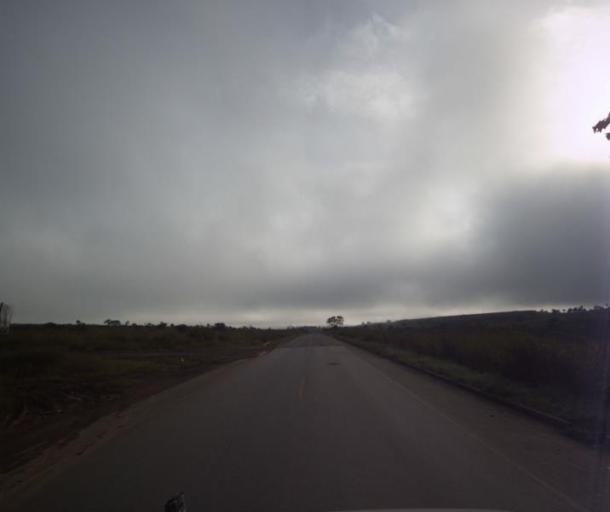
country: BR
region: Goias
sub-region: Pirenopolis
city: Pirenopolis
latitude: -15.7676
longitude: -48.7598
